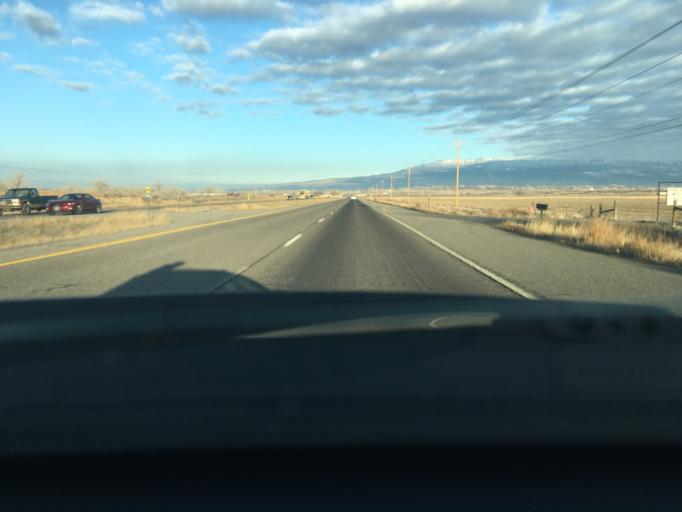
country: US
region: Colorado
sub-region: Delta County
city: Delta
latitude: 38.6891
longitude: -108.0139
